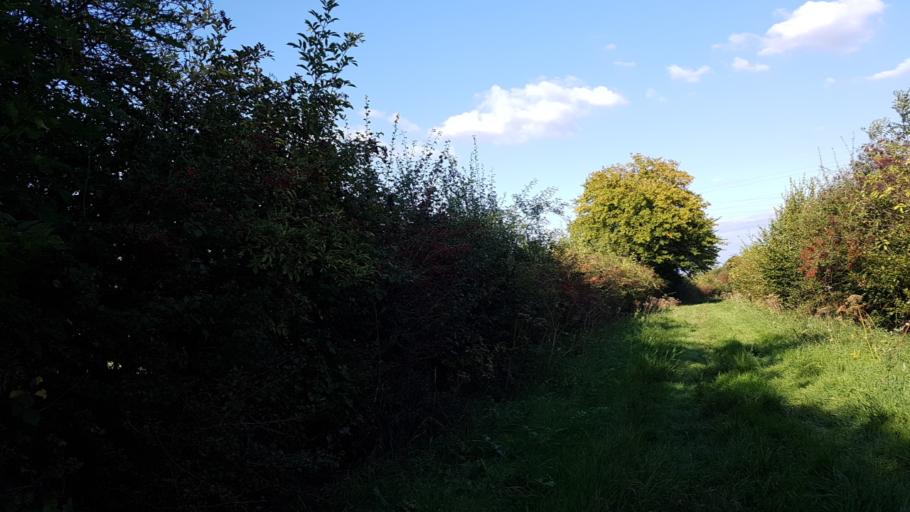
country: FR
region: Picardie
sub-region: Departement de l'Aisne
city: La Capelle
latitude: 49.9802
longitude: 3.9267
